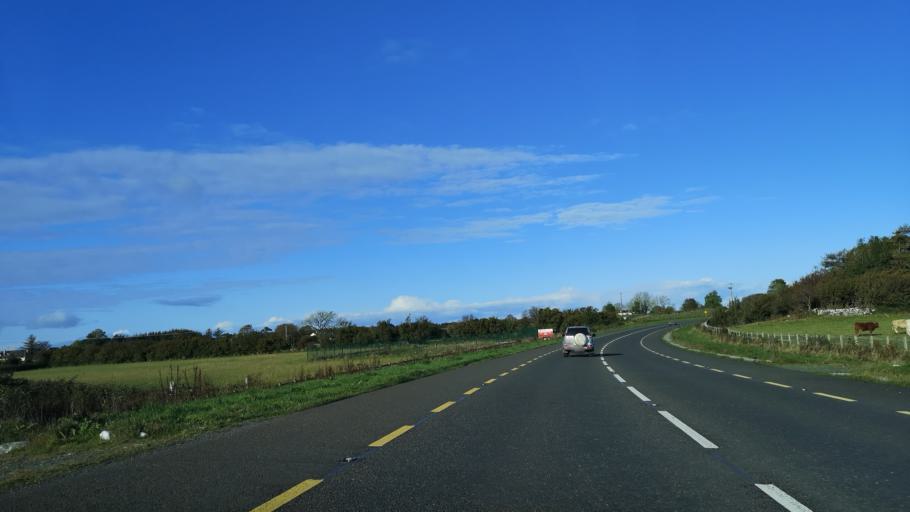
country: IE
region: Connaught
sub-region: County Galway
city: Claregalway
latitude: 53.4282
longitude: -9.0516
